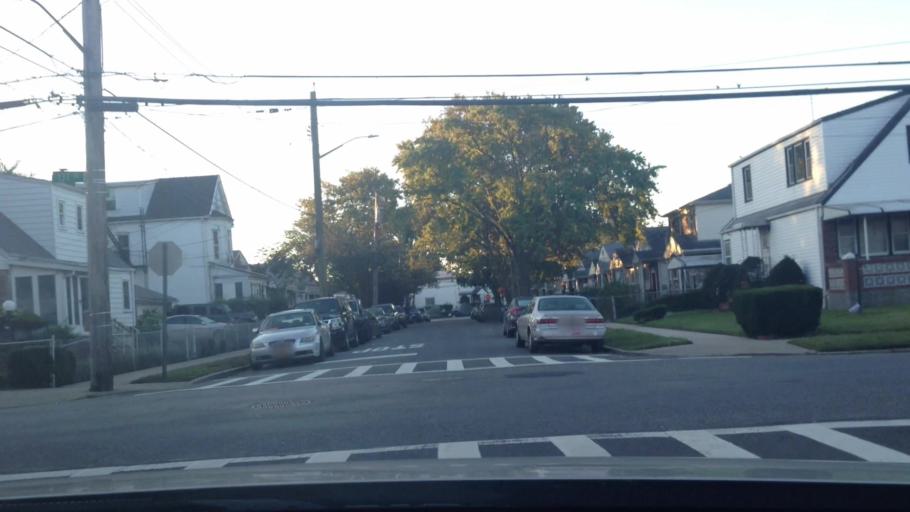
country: US
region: New York
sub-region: Queens County
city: Jamaica
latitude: 40.6705
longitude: -73.7779
